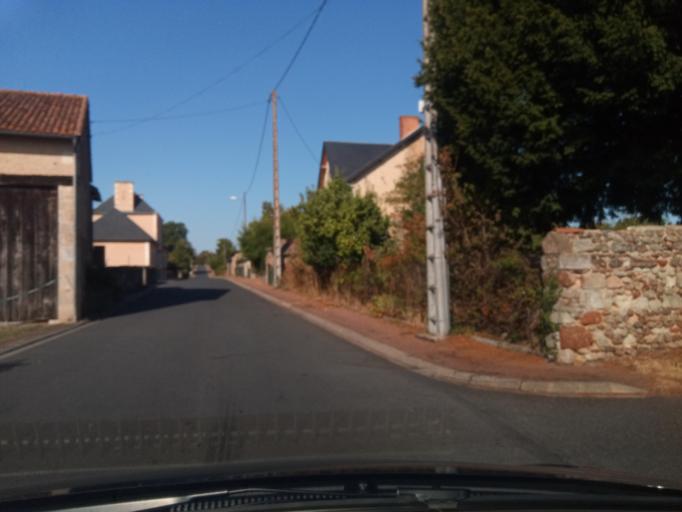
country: FR
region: Poitou-Charentes
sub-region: Departement de la Vienne
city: Saulge
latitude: 46.3319
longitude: 0.8722
